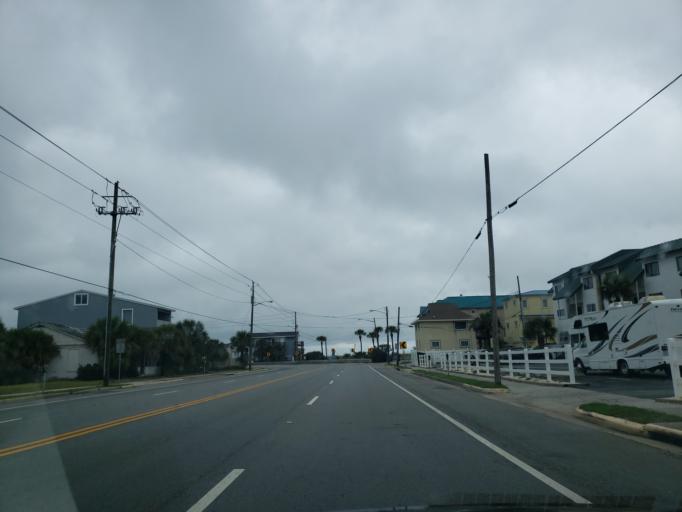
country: US
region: Georgia
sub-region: Chatham County
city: Tybee Island
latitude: 32.0113
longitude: -80.8415
